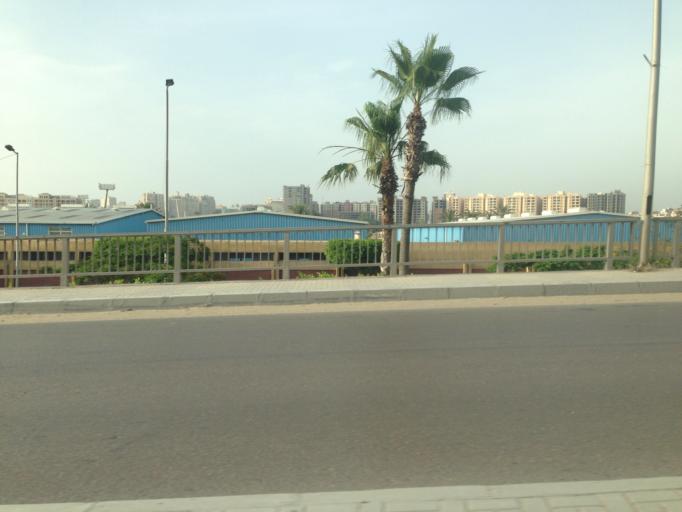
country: EG
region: Alexandria
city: Alexandria
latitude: 31.2114
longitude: 29.9563
